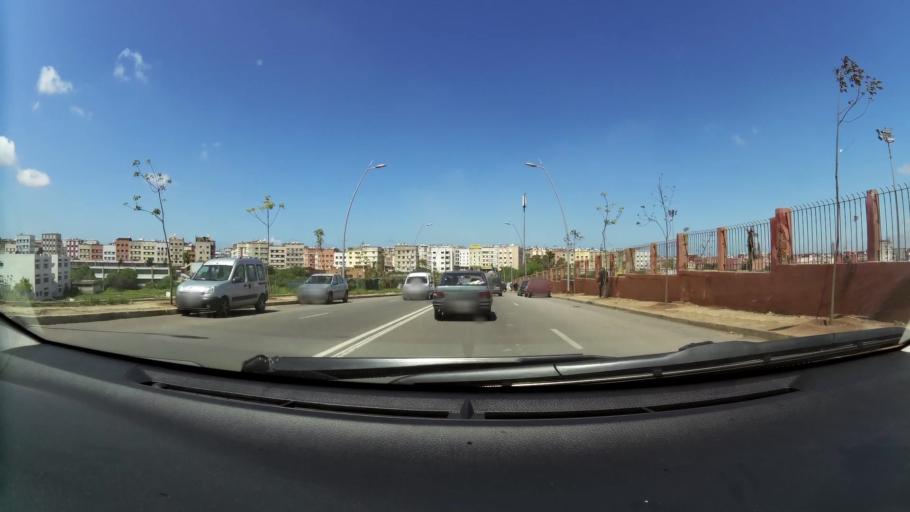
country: MA
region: Grand Casablanca
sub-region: Casablanca
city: Casablanca
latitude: 33.5611
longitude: -7.5878
